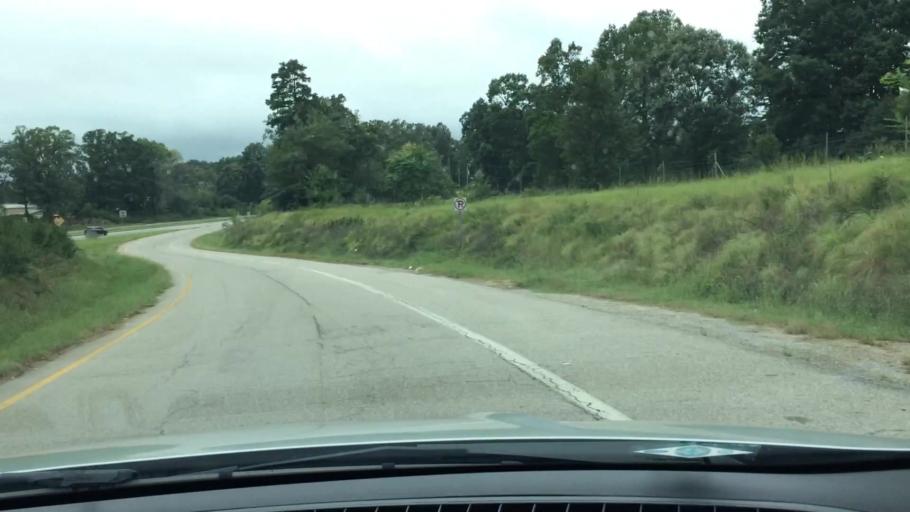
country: US
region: Virginia
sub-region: Pittsylvania County
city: Chatham
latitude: 36.8496
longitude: -79.3929
